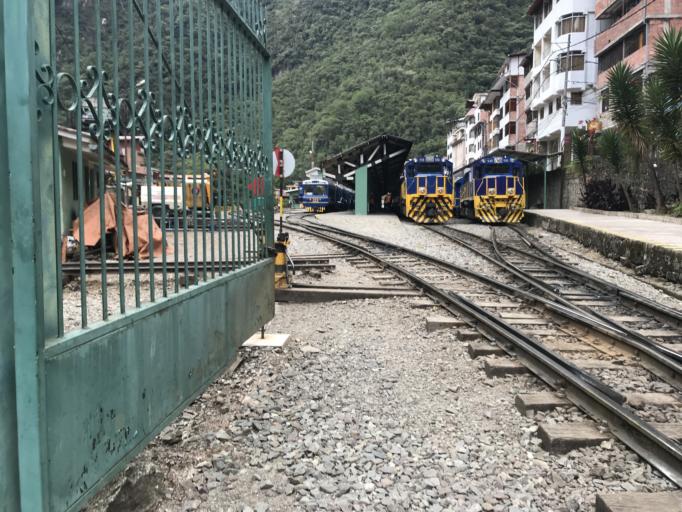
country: PE
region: Cusco
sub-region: Provincia de La Convencion
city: Santa Teresa
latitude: -13.1569
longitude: -72.5238
